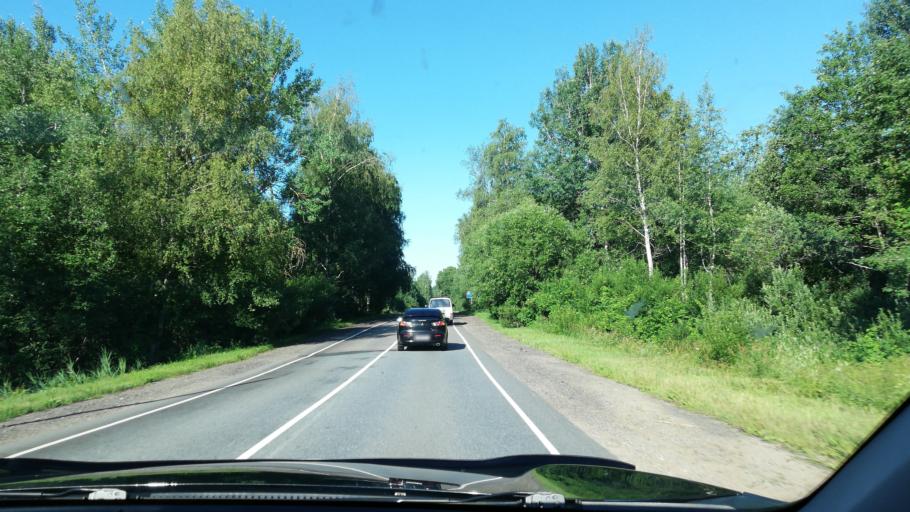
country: RU
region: Pskov
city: Nevel'
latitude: 56.0312
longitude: 30.1148
